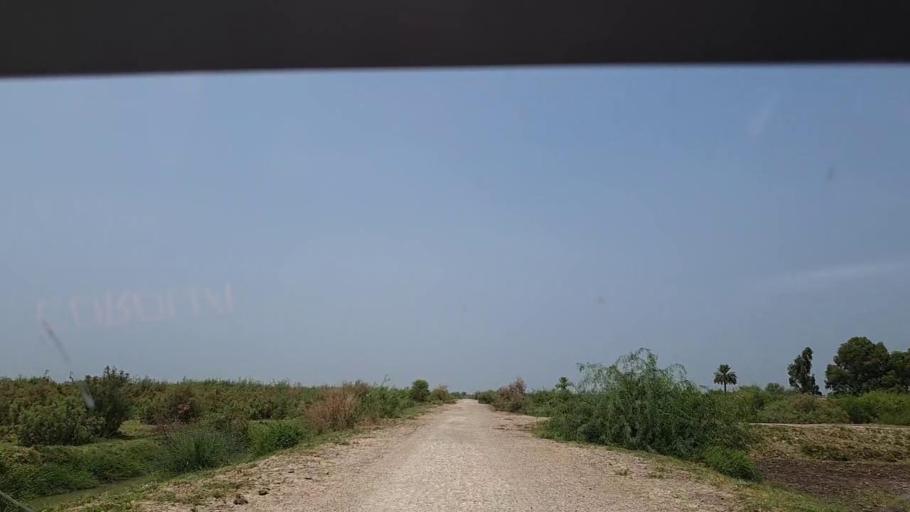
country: PK
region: Sindh
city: Adilpur
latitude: 27.8944
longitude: 69.2439
